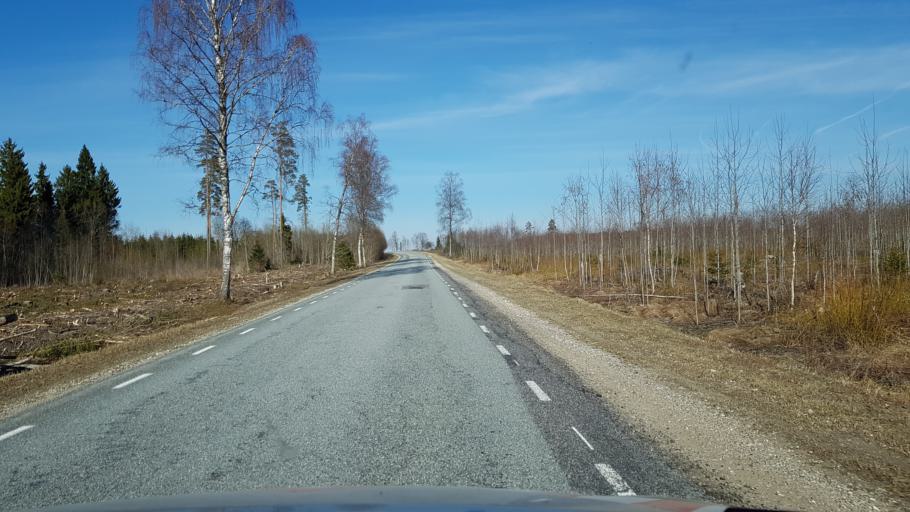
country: EE
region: Laeaene-Virumaa
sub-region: Rakke vald
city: Rakke
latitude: 59.0178
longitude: 26.3486
